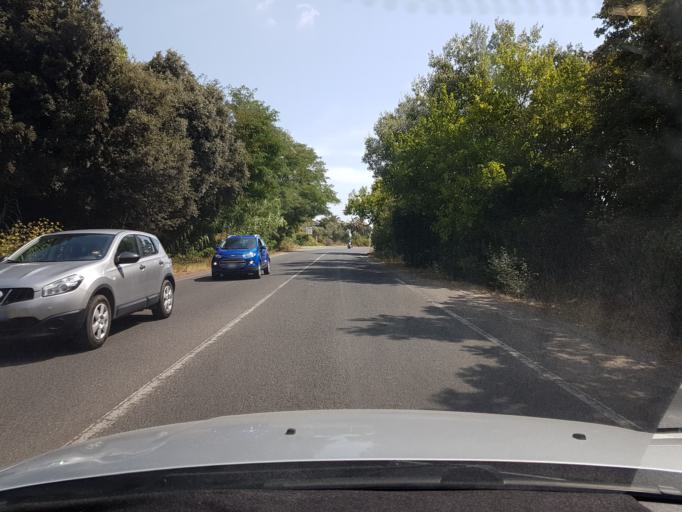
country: IT
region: Sardinia
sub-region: Provincia di Oristano
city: Donigala Fenugheddu
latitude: 39.9216
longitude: 8.5673
